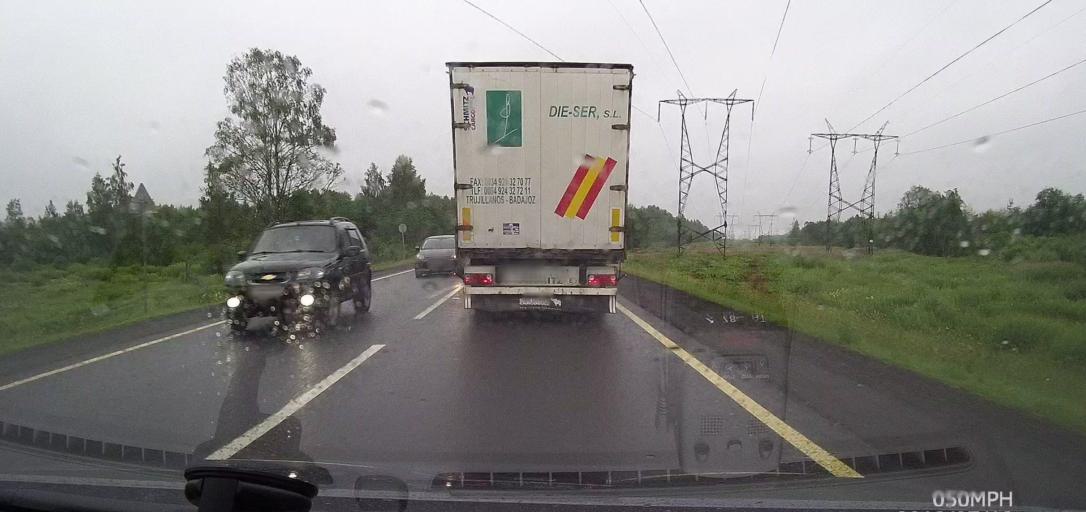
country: RU
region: Leningrad
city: Staraya Ladoga
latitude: 60.0326
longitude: 32.2178
